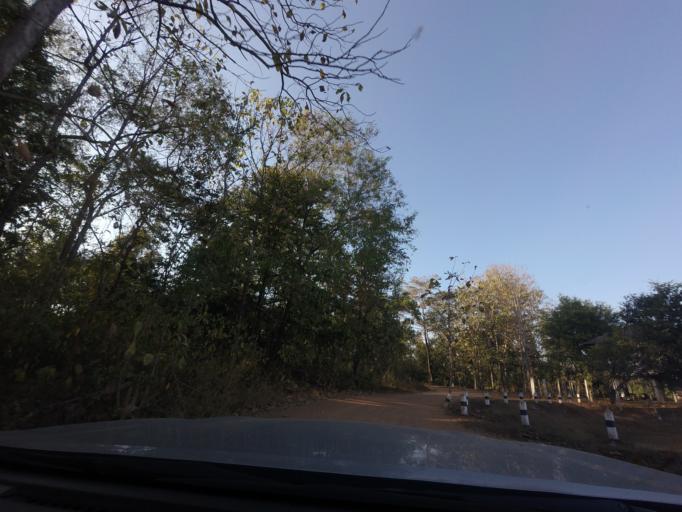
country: TH
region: Lampang
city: Mae Mo
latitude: 18.4132
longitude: 99.7450
